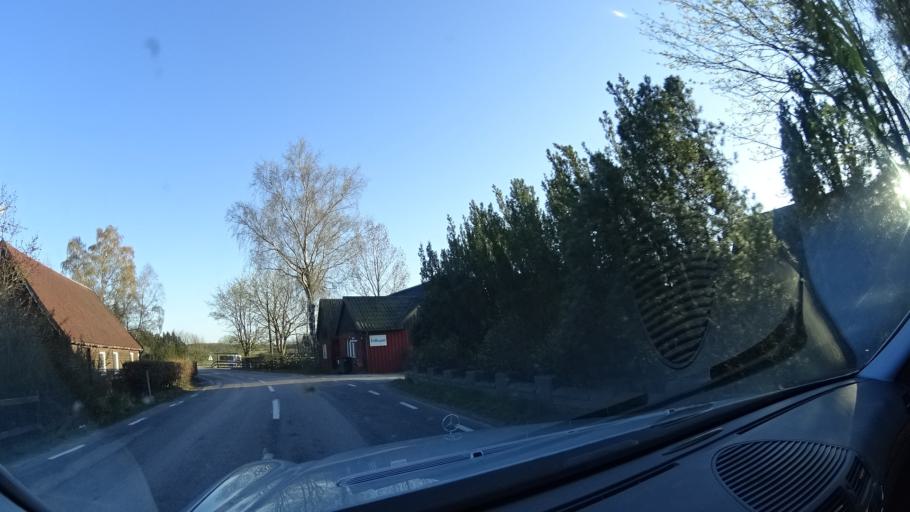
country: SE
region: Skane
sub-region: Bjuvs Kommun
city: Billesholm
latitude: 56.0419
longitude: 13.0126
